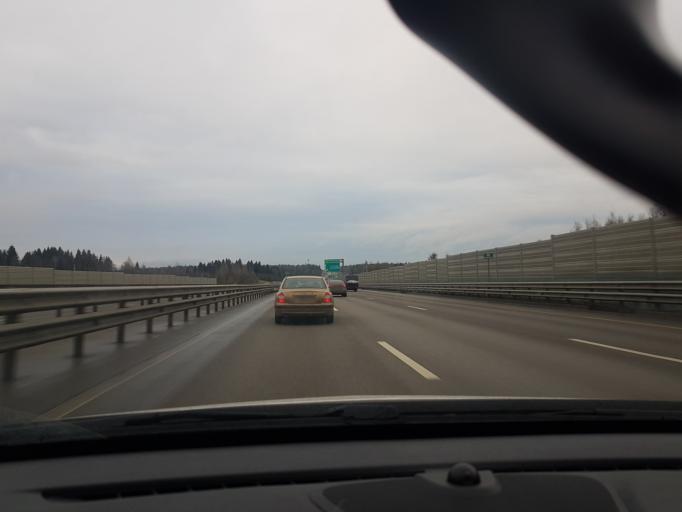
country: RU
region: Moskovskaya
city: Kostrovo
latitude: 55.8818
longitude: 36.6692
